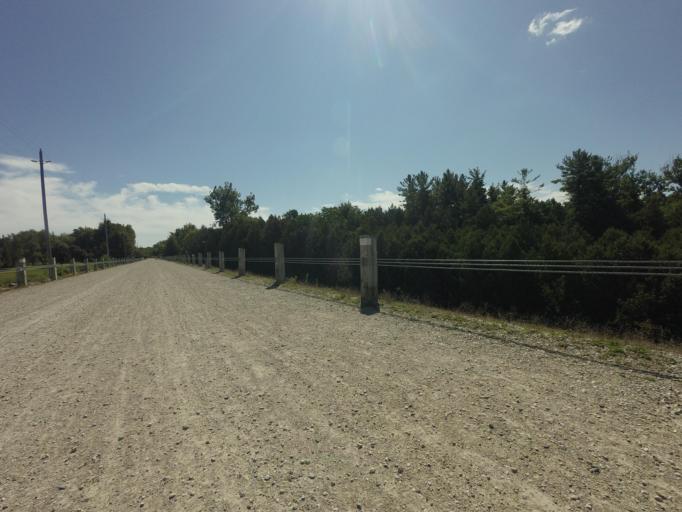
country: CA
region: Ontario
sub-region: Wellington County
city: Guelph
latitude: 43.7340
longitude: -80.3359
